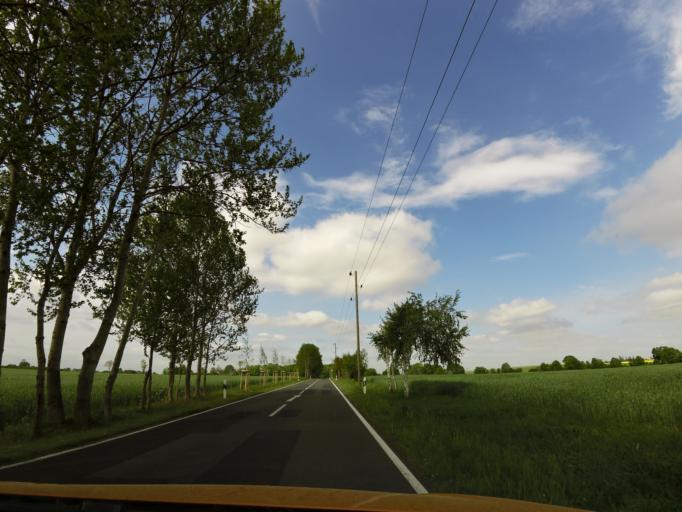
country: DE
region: Brandenburg
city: Belzig
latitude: 52.0935
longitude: 12.5832
